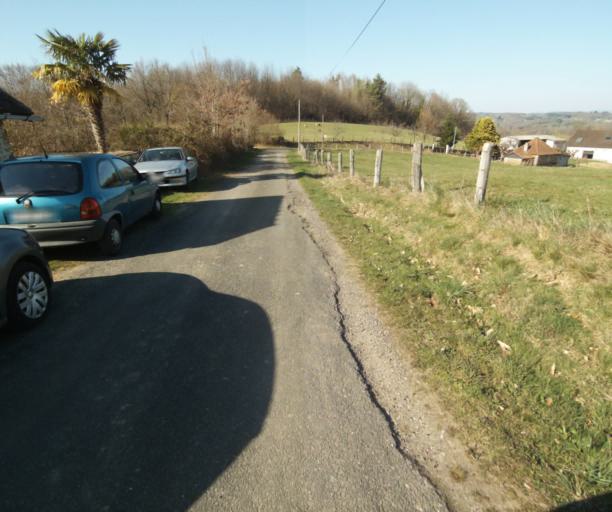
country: FR
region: Limousin
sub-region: Departement de la Correze
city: Saint-Clement
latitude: 45.3115
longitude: 1.6889
